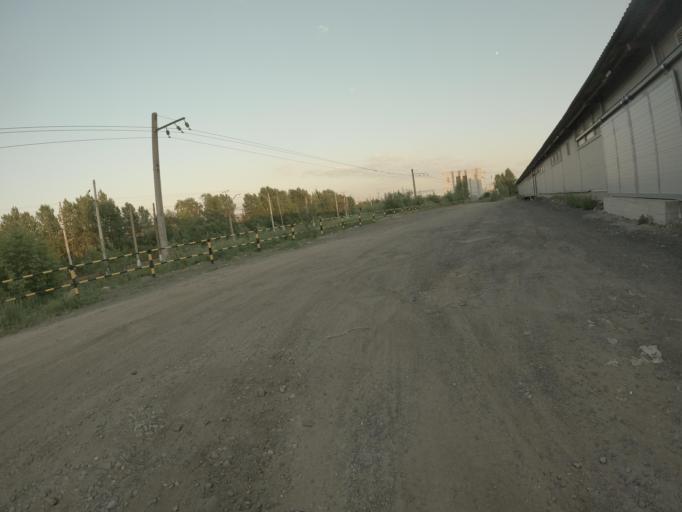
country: RU
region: St.-Petersburg
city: Admiralteisky
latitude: 59.8852
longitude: 30.2933
